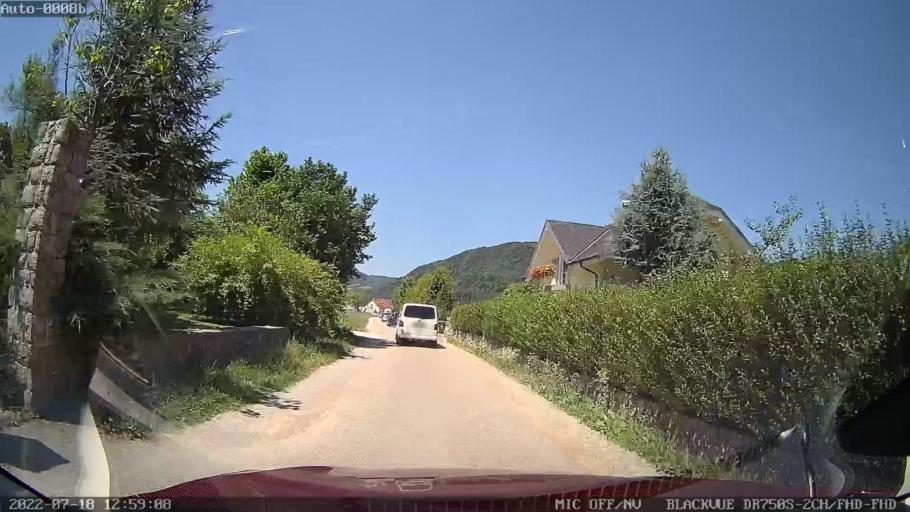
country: SI
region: Dobrova-Horjul-Polhov Gradec
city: Dobrova
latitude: 46.0653
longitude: 14.4152
